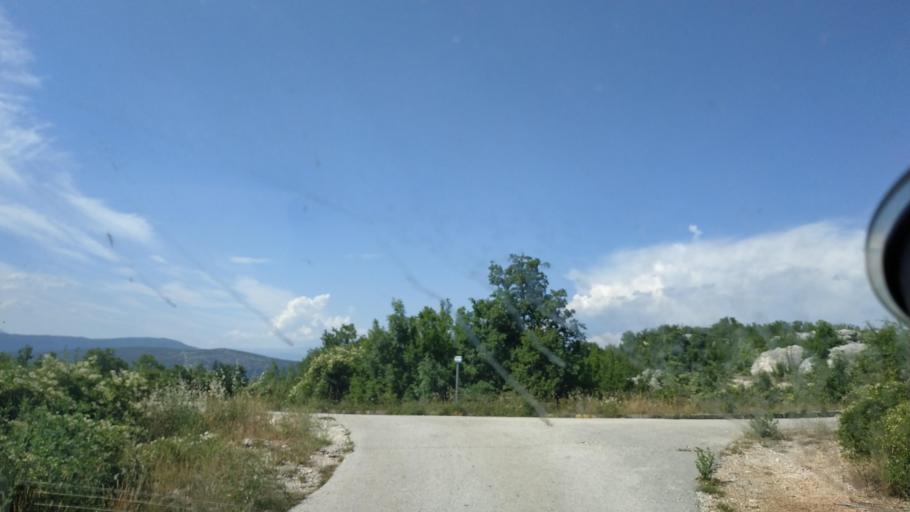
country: HR
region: Splitsko-Dalmatinska
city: Greda
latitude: 43.5788
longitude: 16.6559
